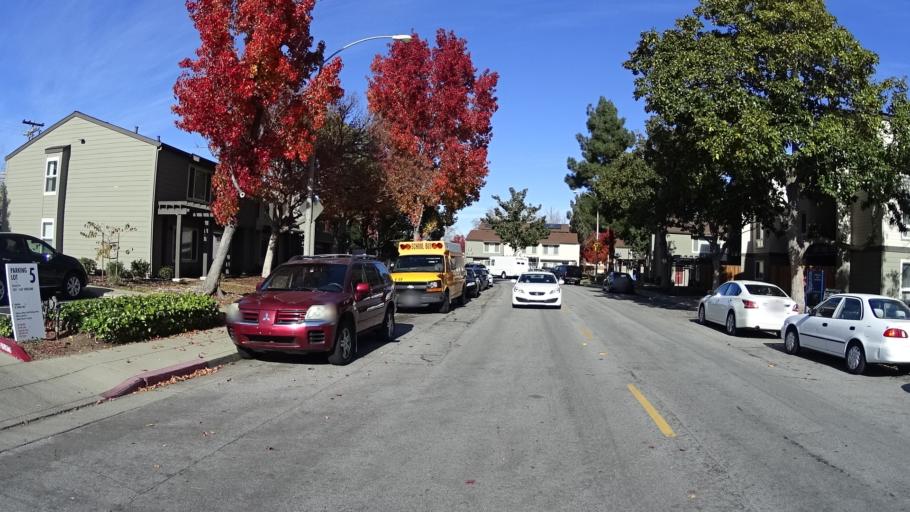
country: US
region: California
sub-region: Santa Clara County
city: Cupertino
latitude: 37.3401
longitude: -122.0365
